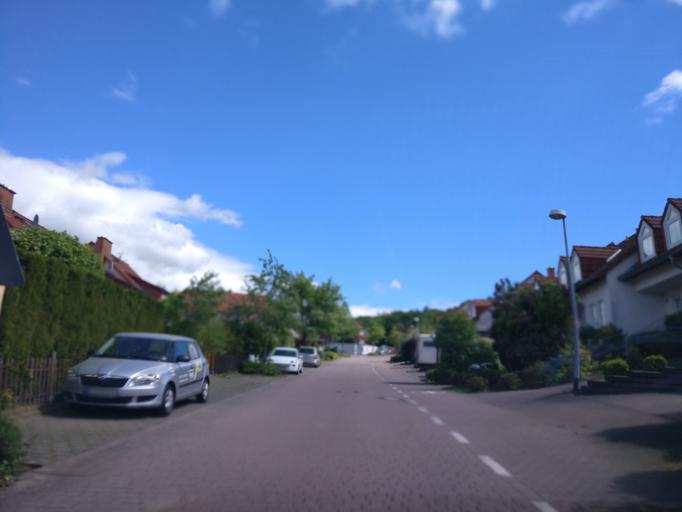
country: DE
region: Lower Saxony
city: Hannoversch Munden
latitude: 51.4018
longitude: 9.6646
